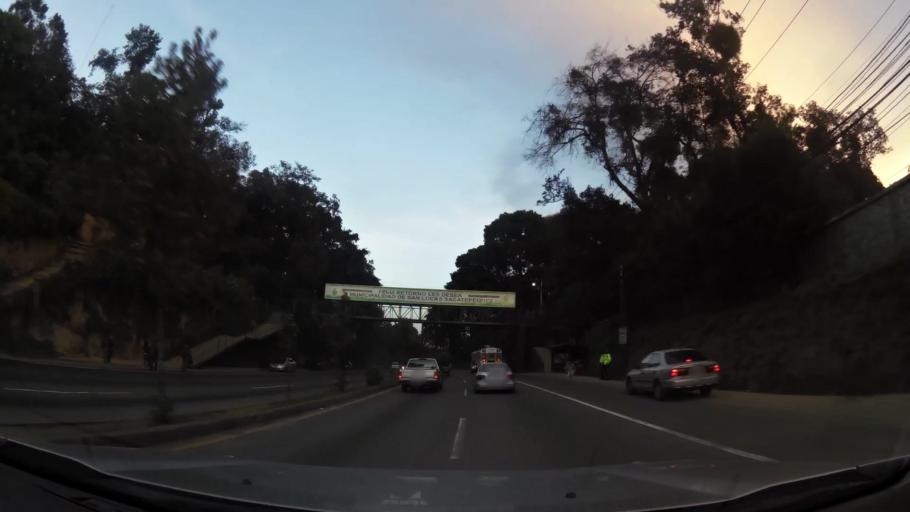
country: GT
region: Sacatepequez
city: San Lucas Sacatepequez
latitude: 14.5994
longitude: -90.6395
